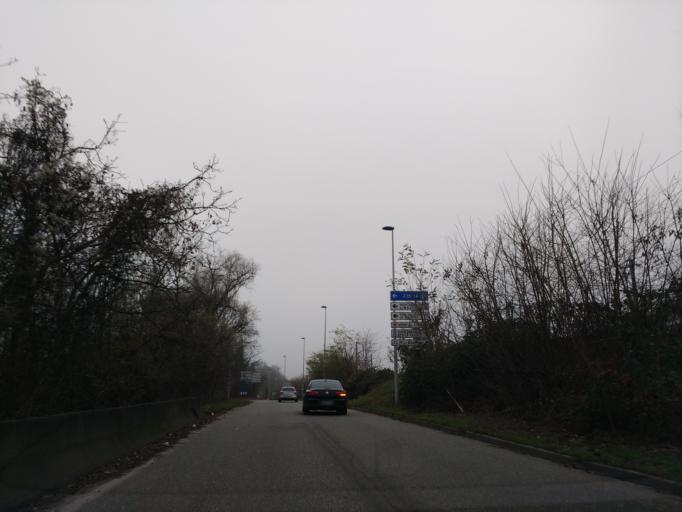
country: FR
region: Alsace
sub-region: Departement du Bas-Rhin
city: Strasbourg
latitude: 48.5710
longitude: 7.7394
